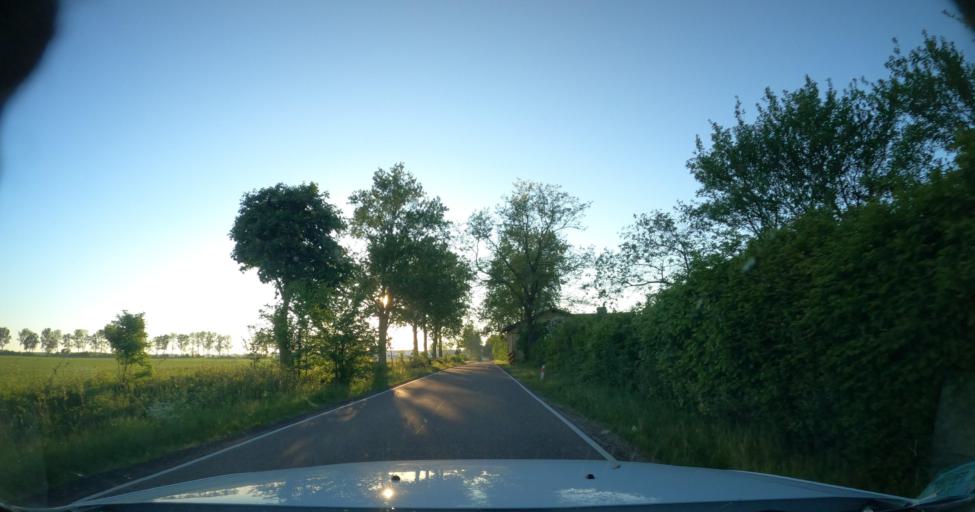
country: PL
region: Pomeranian Voivodeship
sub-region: Powiat slupski
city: Potegowo
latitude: 54.4091
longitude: 17.4229
